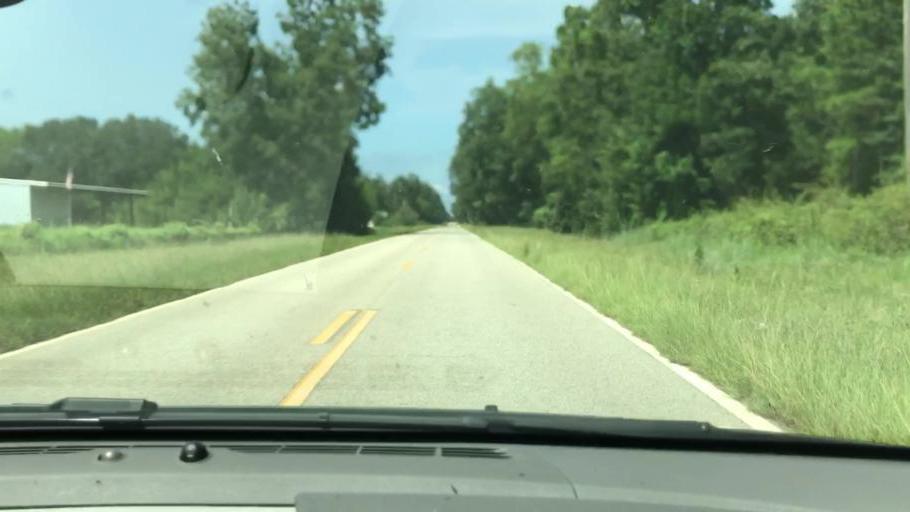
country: US
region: Georgia
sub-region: Seminole County
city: Donalsonville
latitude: 31.1334
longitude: -84.9953
